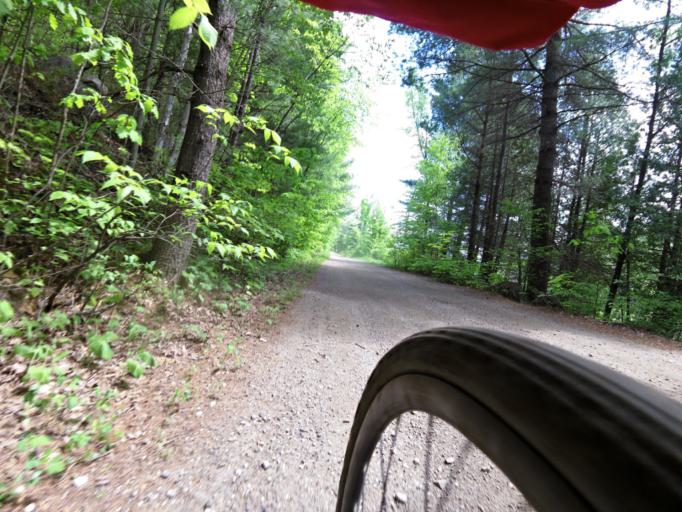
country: CA
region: Ontario
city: Renfrew
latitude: 45.2068
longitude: -76.6899
